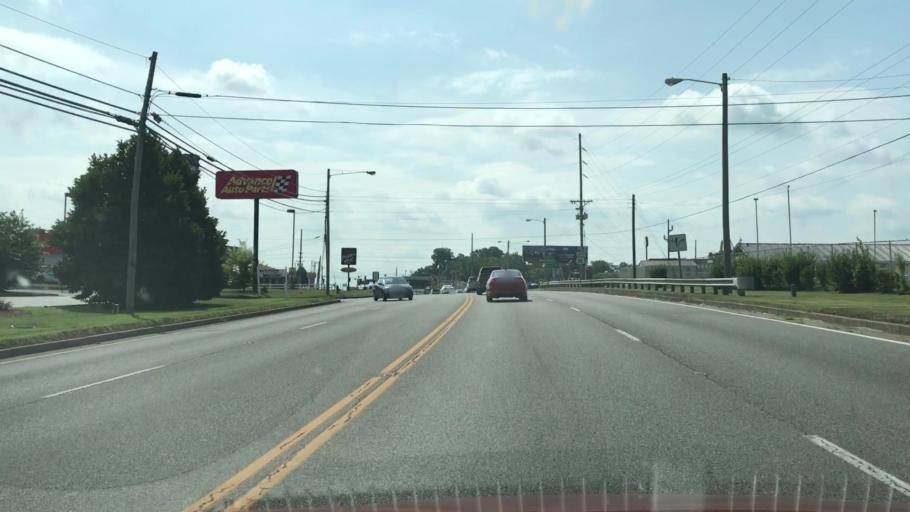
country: US
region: Kentucky
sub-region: Barren County
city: Glasgow
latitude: 37.0110
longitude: -85.9242
